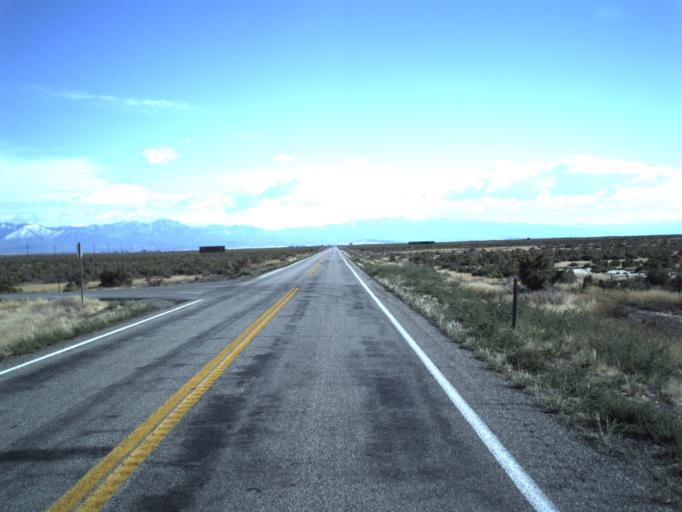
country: US
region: Utah
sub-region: Millard County
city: Delta
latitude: 39.2874
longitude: -112.4642
